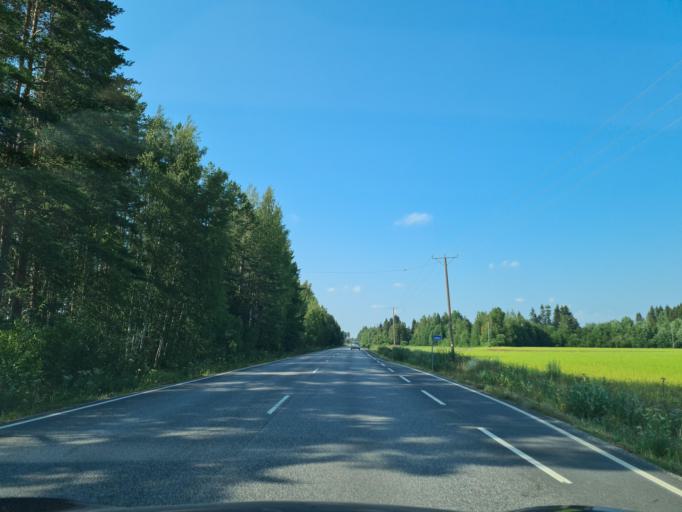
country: FI
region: Satakunta
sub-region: Pohjois-Satakunta
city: Karvia
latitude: 61.9642
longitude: 22.5088
